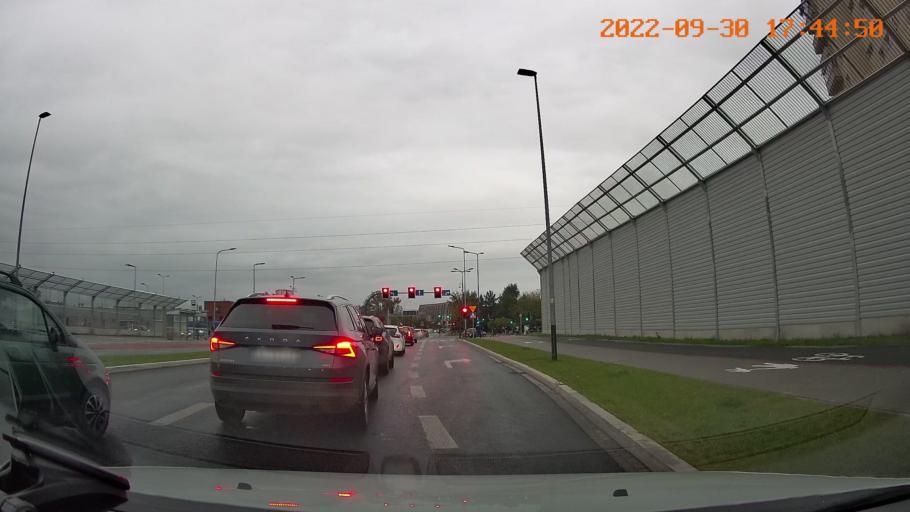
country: PL
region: Lesser Poland Voivodeship
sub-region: Krakow
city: Krakow
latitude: 50.0291
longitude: 19.9137
